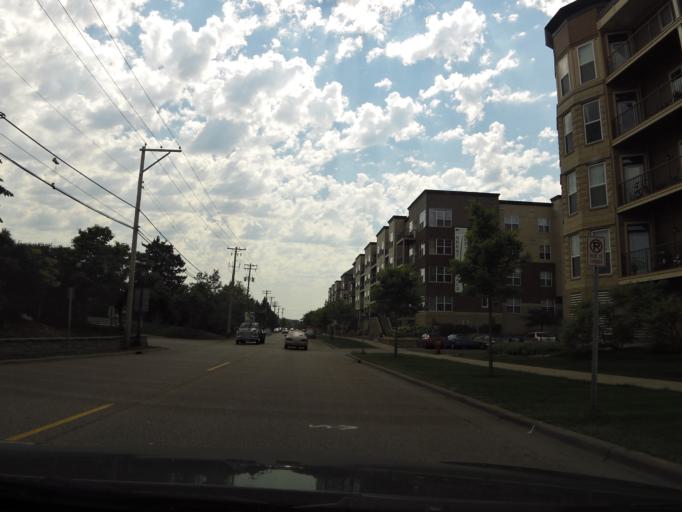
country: US
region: Minnesota
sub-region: Dakota County
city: Mendota Heights
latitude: 44.9003
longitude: -93.1722
